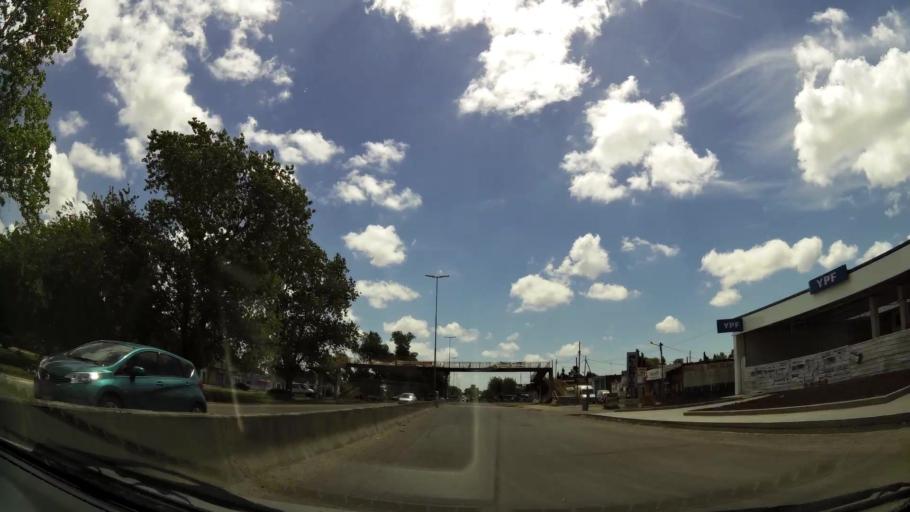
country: AR
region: Buenos Aires
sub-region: Partido de Quilmes
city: Quilmes
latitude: -34.8145
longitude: -58.2282
